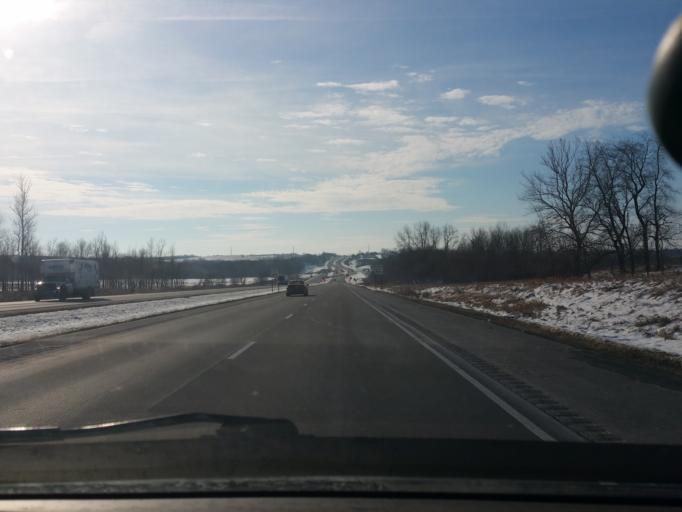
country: US
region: Iowa
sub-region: Warren County
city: Norwalk
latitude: 41.4306
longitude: -93.7808
